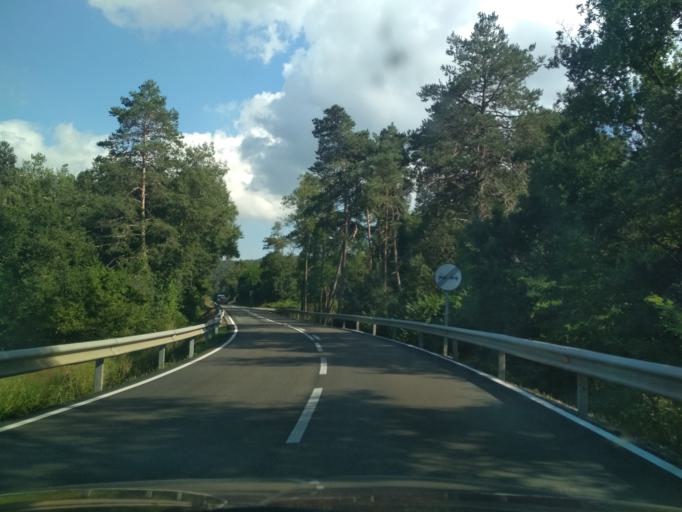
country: ES
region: Catalonia
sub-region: Provincia de Barcelona
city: Sant Quirze Safaja
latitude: 41.7354
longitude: 2.1351
